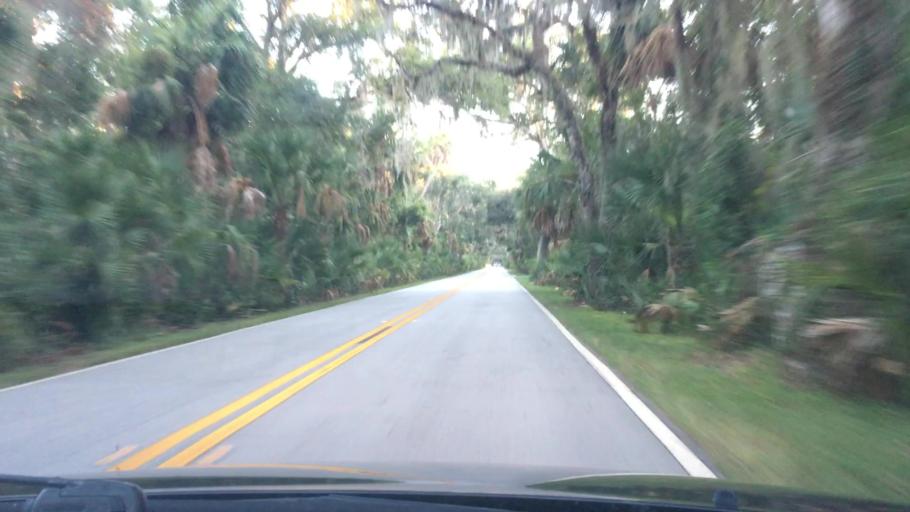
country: US
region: Florida
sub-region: Volusia County
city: Ormond-by-the-Sea
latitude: 29.3366
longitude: -81.0817
